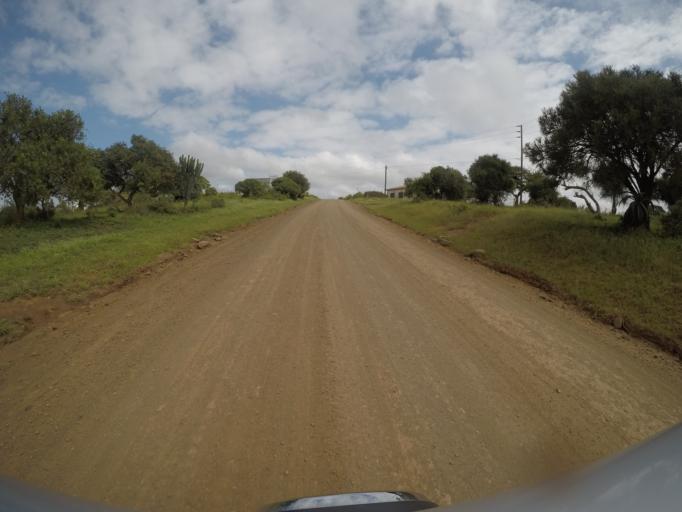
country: ZA
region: KwaZulu-Natal
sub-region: uThungulu District Municipality
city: Empangeni
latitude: -28.6044
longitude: 31.8482
